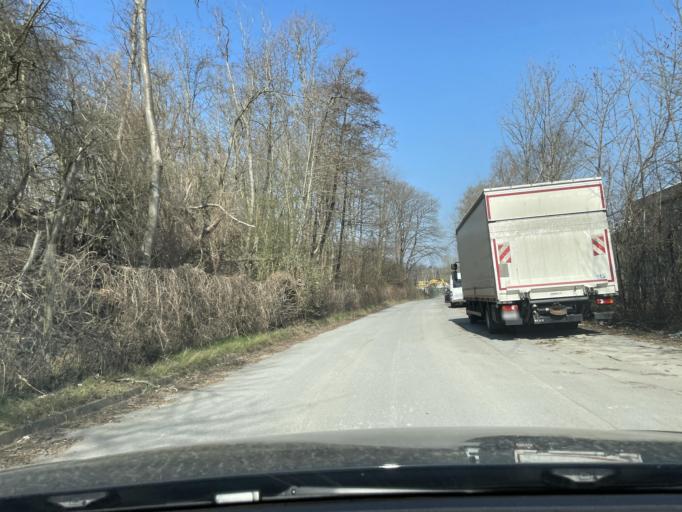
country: DE
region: North Rhine-Westphalia
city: Wulfrath
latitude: 51.2446
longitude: 7.0568
